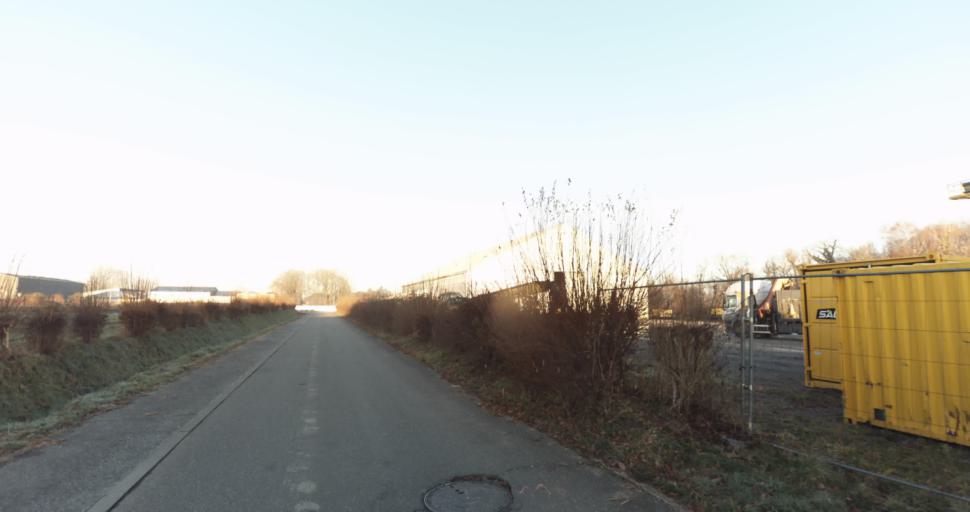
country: FR
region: Aquitaine
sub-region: Departement des Pyrenees-Atlantiques
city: Buros
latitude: 43.3229
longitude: -0.2912
